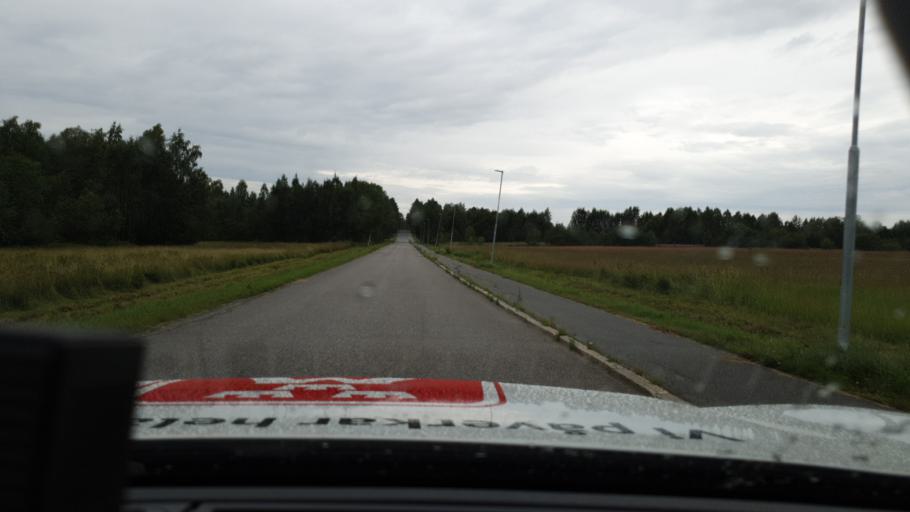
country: SE
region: Norrbotten
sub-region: Lulea Kommun
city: Sodra Sunderbyn
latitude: 65.6696
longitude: 21.9035
